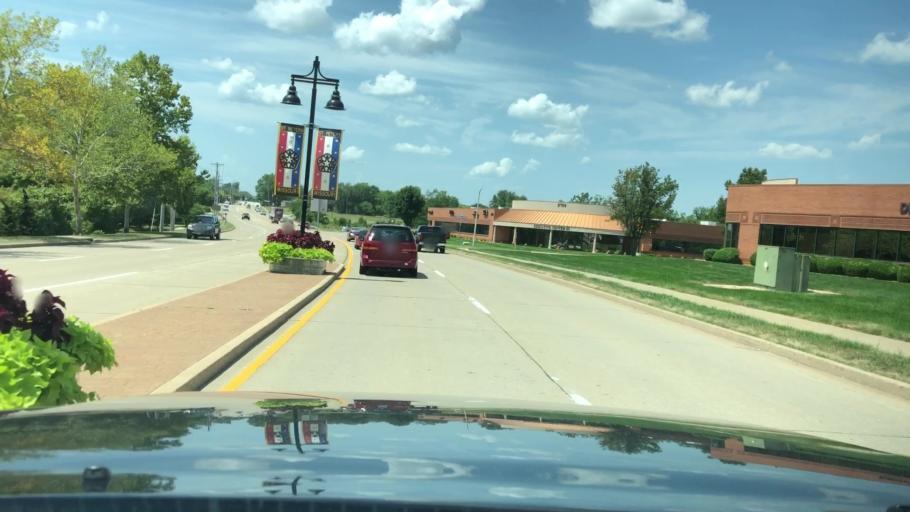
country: US
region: Missouri
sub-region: Saint Charles County
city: Saint Peters
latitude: 38.7927
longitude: -90.5988
